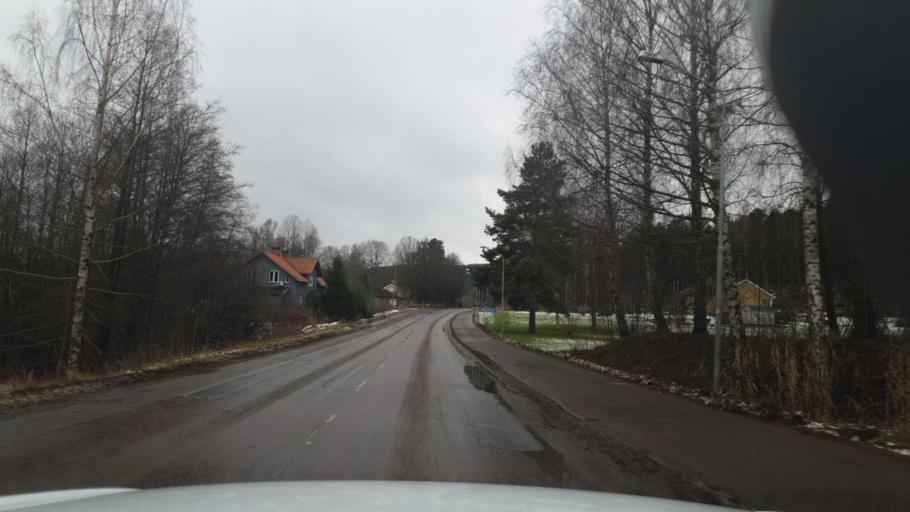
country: SE
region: Vaermland
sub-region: Eda Kommun
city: Amotfors
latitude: 59.7609
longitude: 12.3599
